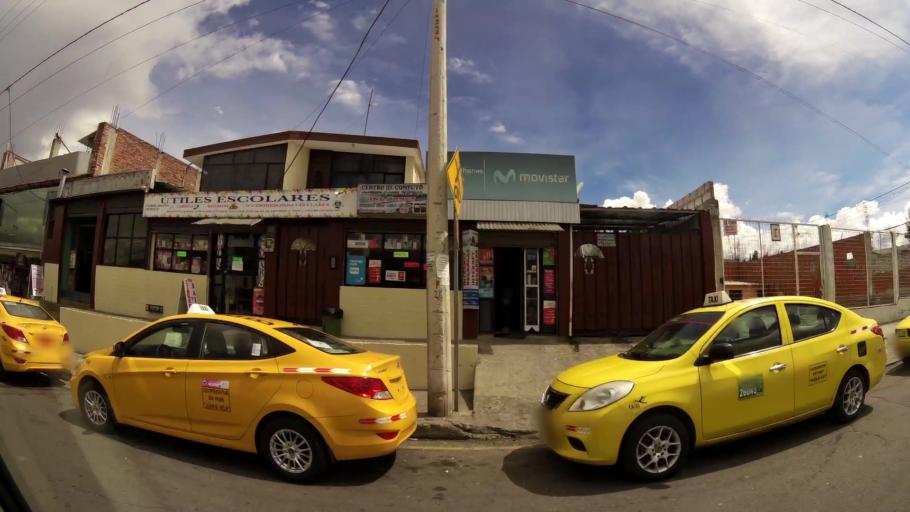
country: EC
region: Tungurahua
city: Ambato
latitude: -1.2703
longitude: -78.6178
